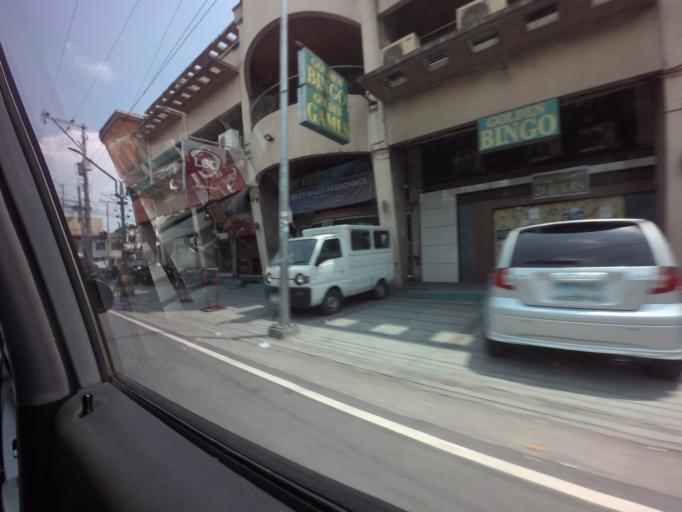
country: PH
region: Metro Manila
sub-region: City of Manila
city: Quiapo
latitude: 14.5912
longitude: 121.0054
